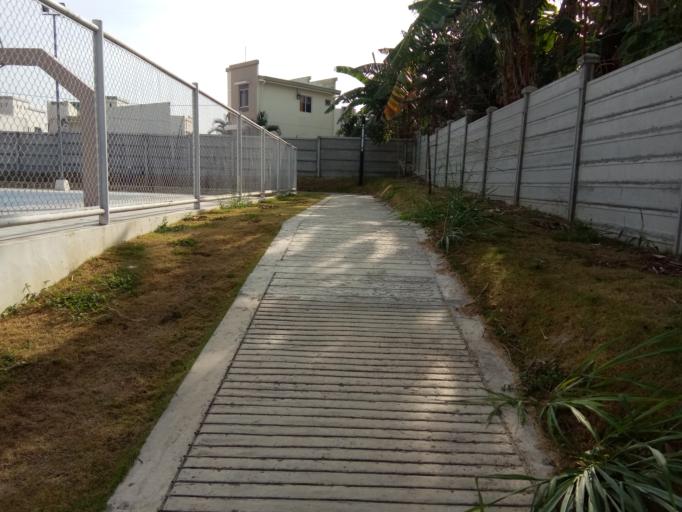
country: PH
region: Calabarzon
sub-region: Province of Cavite
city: Biga
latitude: 14.2767
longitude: 120.9708
